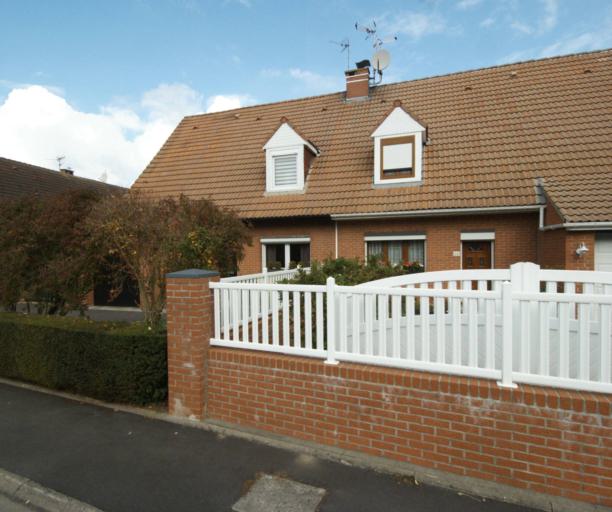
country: FR
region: Nord-Pas-de-Calais
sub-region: Departement du Nord
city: Herlies
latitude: 50.5786
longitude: 2.8615
